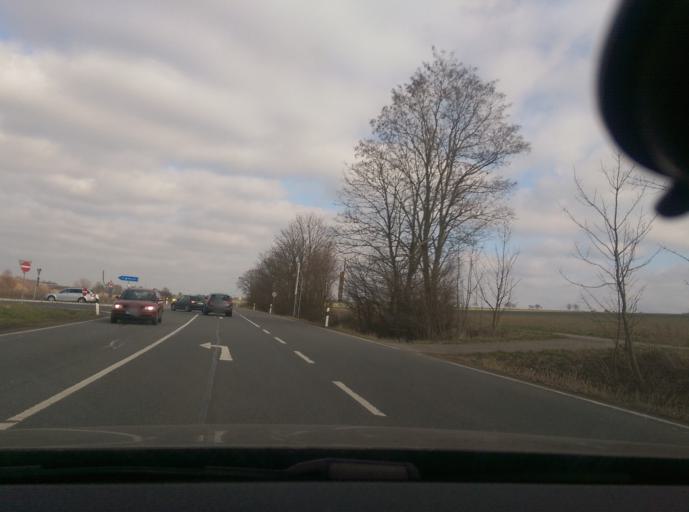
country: DE
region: Lower Saxony
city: Rehren
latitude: 52.2312
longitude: 9.2478
